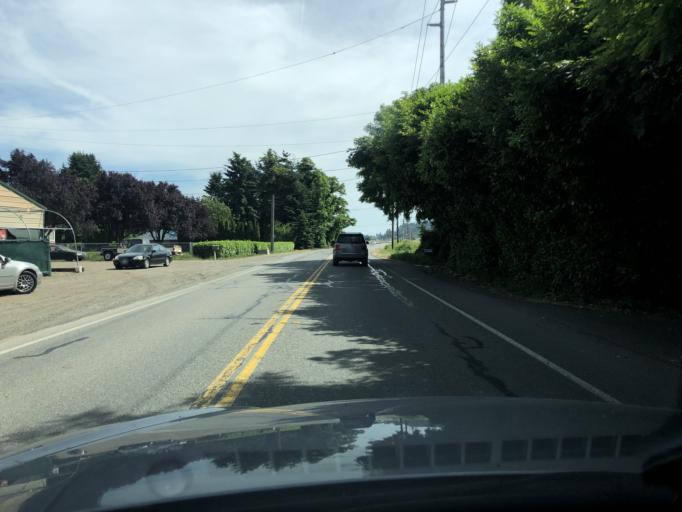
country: US
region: Washington
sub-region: King County
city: Kent
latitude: 47.3648
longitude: -122.2493
